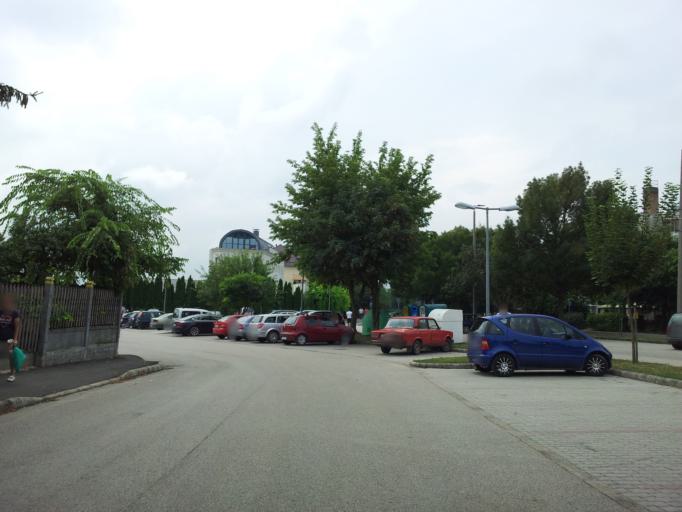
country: HU
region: Tolna
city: Tamasi
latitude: 46.6365
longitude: 18.2820
